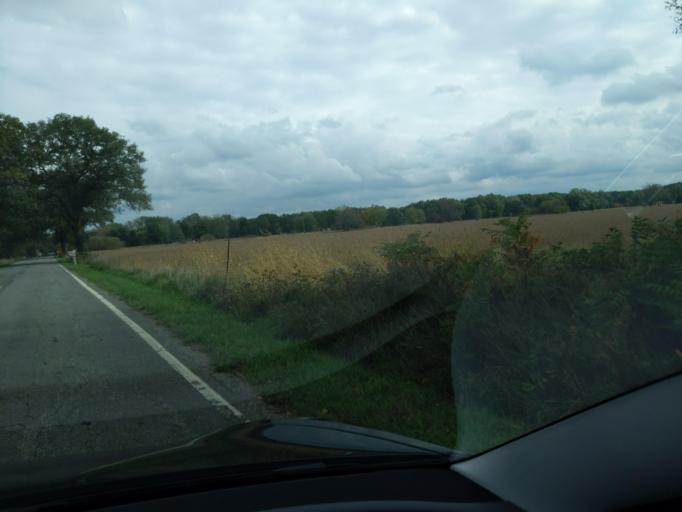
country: US
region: Michigan
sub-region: Ingham County
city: Leslie
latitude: 42.4115
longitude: -84.4482
